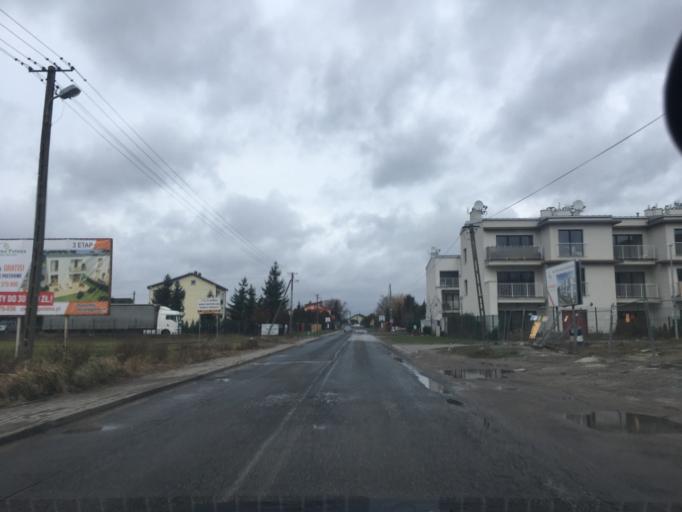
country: PL
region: Masovian Voivodeship
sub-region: Powiat piaseczynski
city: Lesznowola
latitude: 52.1023
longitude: 20.9320
